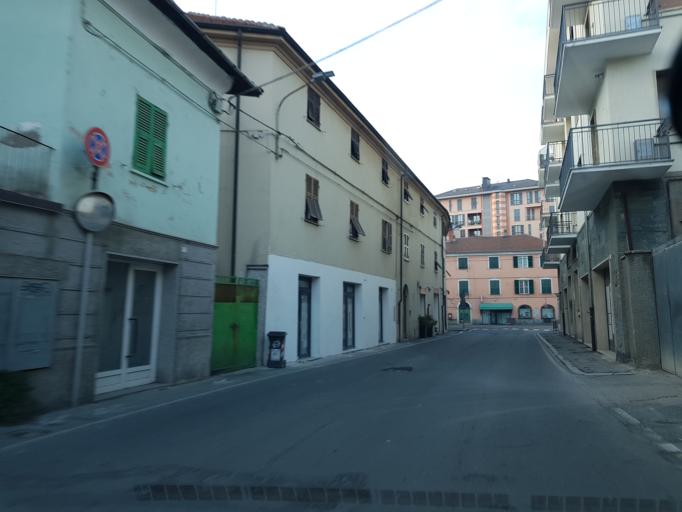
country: IT
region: Piedmont
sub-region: Provincia di Alessandria
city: Novi Ligure
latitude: 44.7601
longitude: 8.7931
